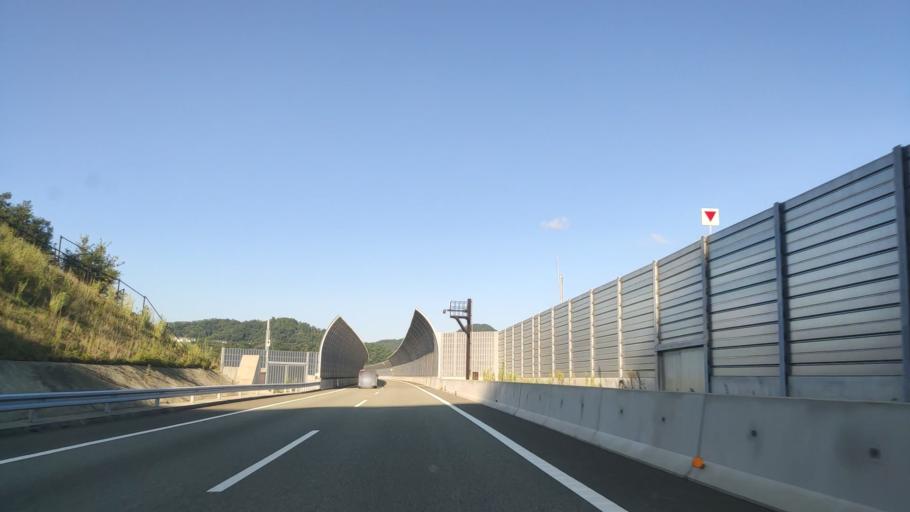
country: JP
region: Hyogo
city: Kawanishi
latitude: 34.8892
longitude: 135.3759
